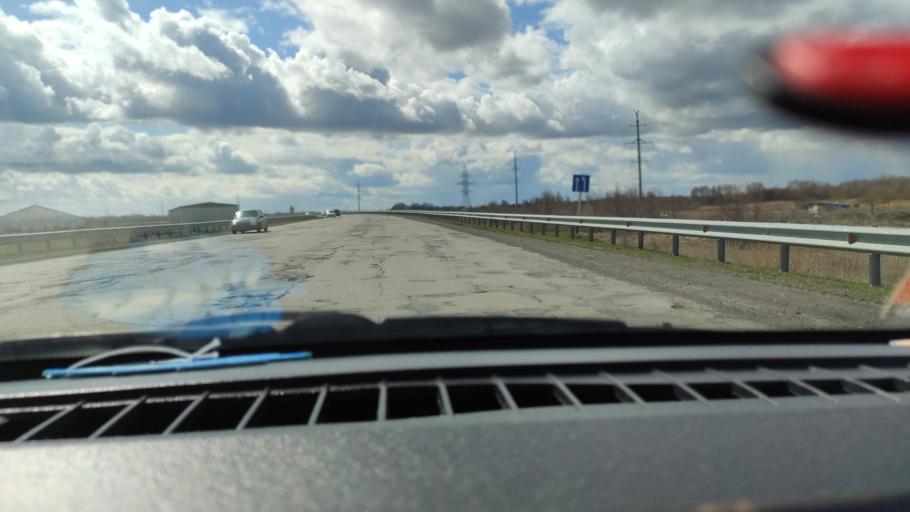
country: RU
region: Samara
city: Tol'yatti
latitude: 53.6692
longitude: 49.4147
